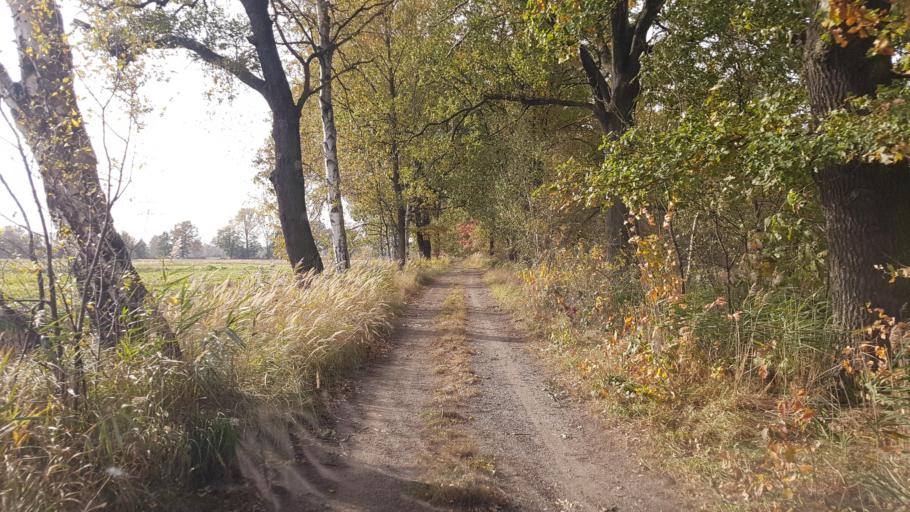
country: DE
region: Brandenburg
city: Schraden
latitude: 51.4530
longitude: 13.7053
